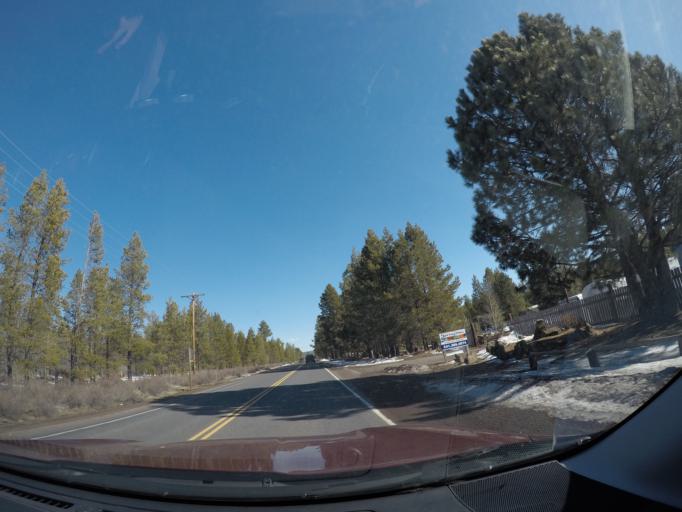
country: US
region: Oregon
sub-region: Deschutes County
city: Sunriver
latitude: 43.8630
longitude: -121.4645
